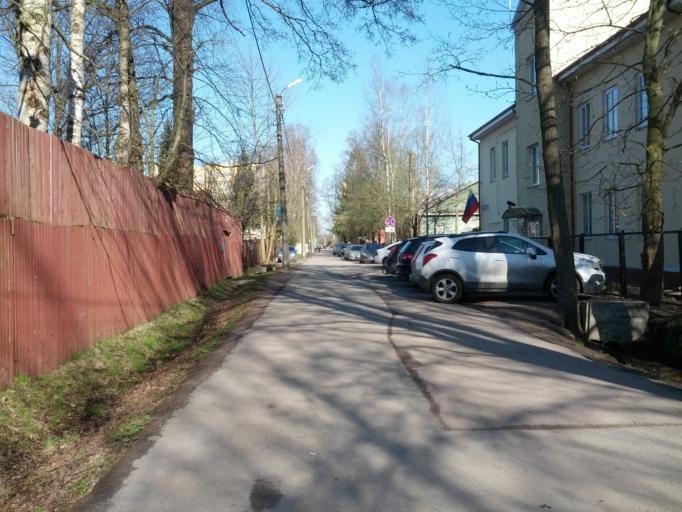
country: RU
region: St.-Petersburg
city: Sestroretsk
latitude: 60.0892
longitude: 29.9431
